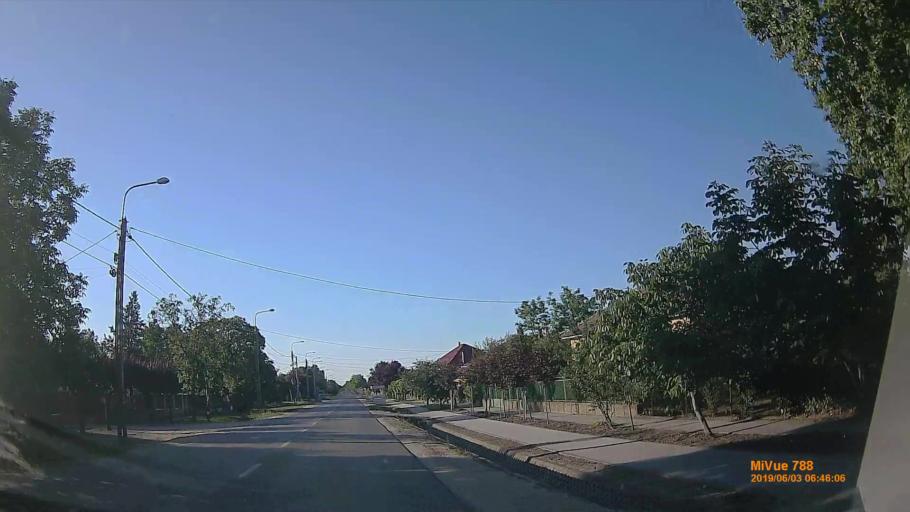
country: HU
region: Pest
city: Bugyi
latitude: 47.2334
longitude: 19.1413
